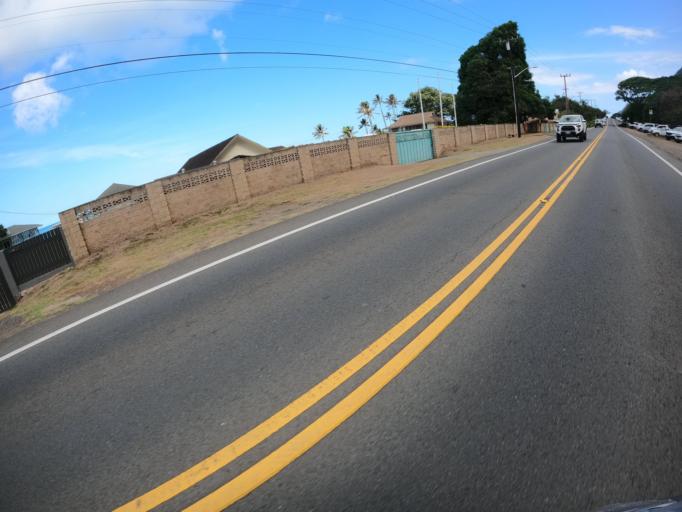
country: US
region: Hawaii
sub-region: Honolulu County
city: Waimanalo Beach
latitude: 21.3247
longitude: -157.6821
